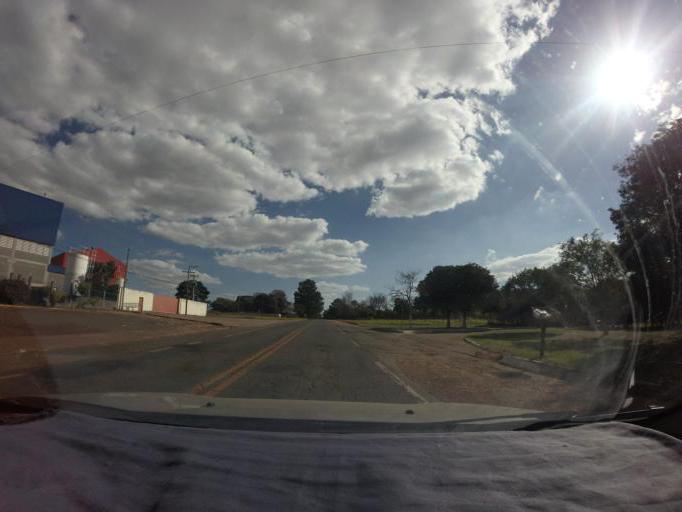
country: BR
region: Sao Paulo
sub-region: Piracicaba
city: Piracicaba
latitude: -22.7396
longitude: -47.5710
